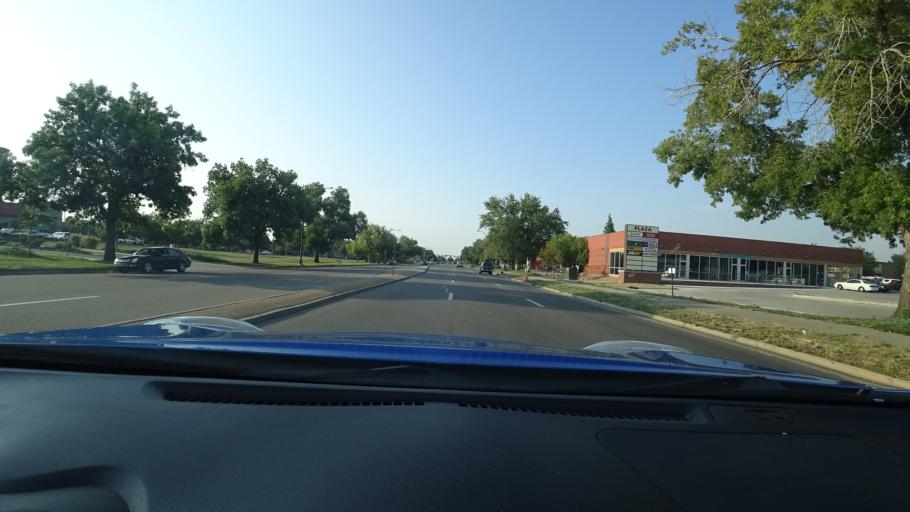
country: US
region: Colorado
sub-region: Adams County
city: Aurora
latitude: 39.7800
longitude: -104.8469
